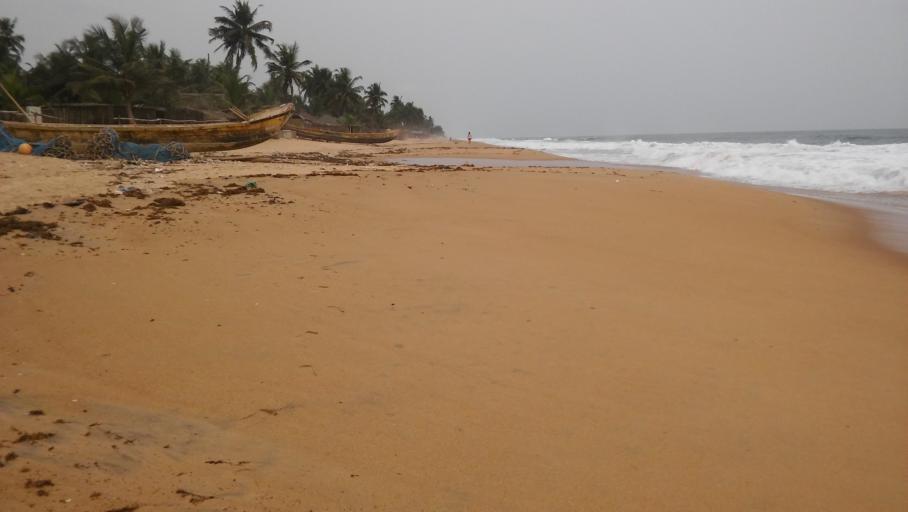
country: CI
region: Sud-Comoe
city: Grand-Bassam
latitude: 5.1981
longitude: -3.7585
